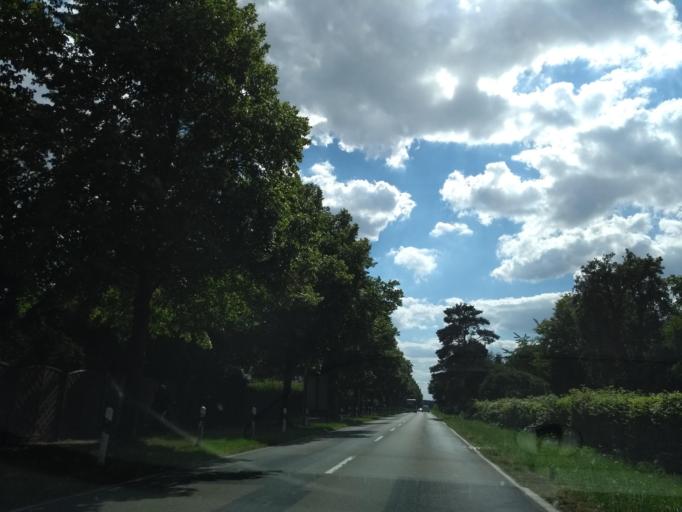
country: DE
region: Lower Saxony
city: Wunstorf
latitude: 52.4238
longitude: 9.4179
